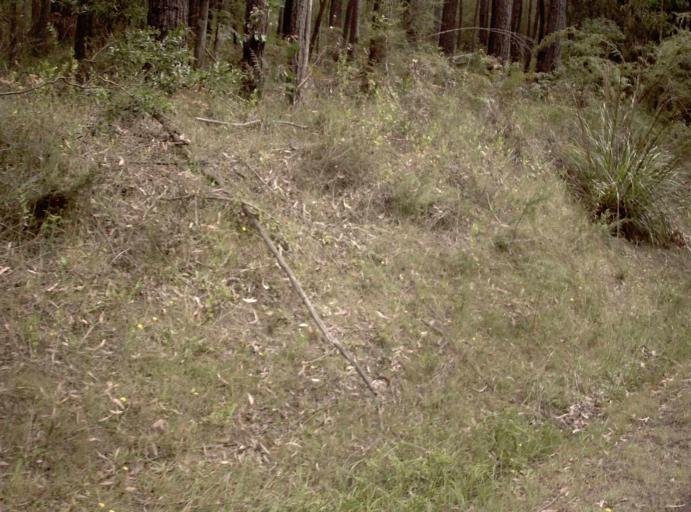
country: AU
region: Victoria
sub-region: Latrobe
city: Morwell
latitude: -38.0754
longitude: 146.4304
